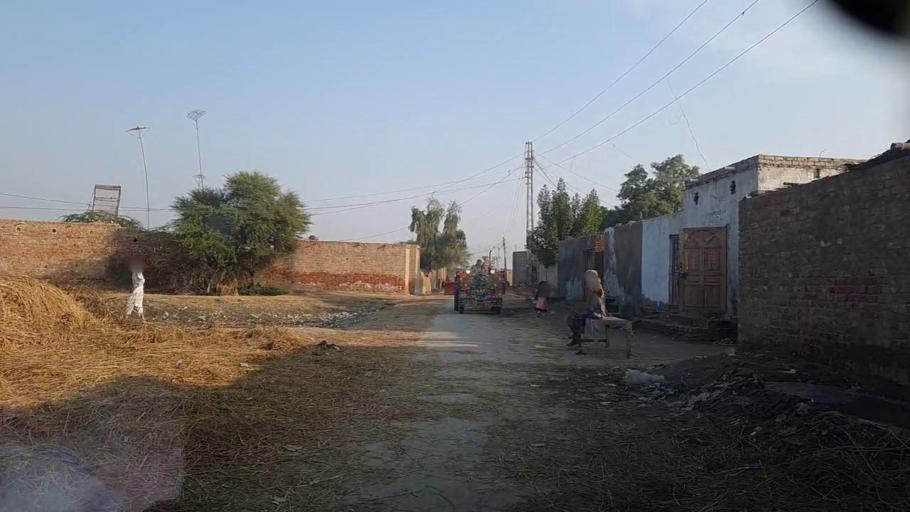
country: PK
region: Sindh
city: Jacobabad
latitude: 28.2384
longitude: 68.4819
